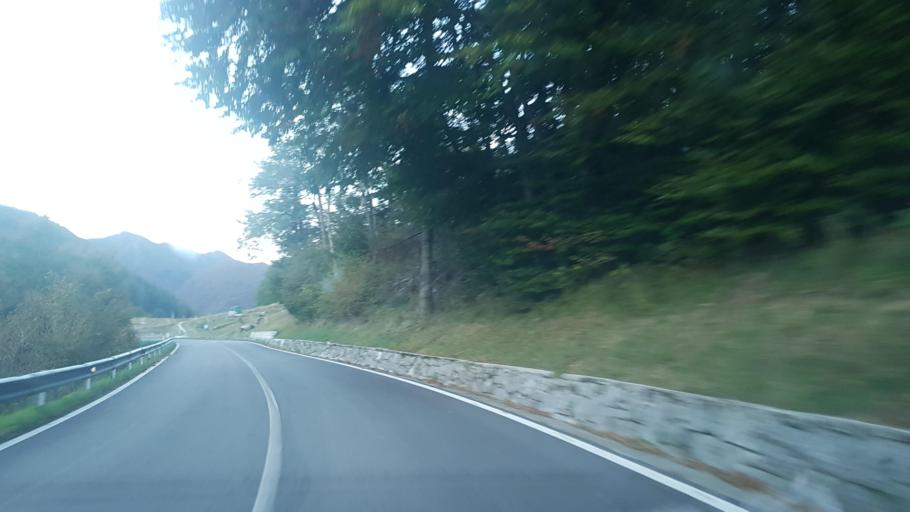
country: IT
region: Friuli Venezia Giulia
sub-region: Provincia di Udine
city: Villa Santina
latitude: 46.3560
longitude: 12.9327
